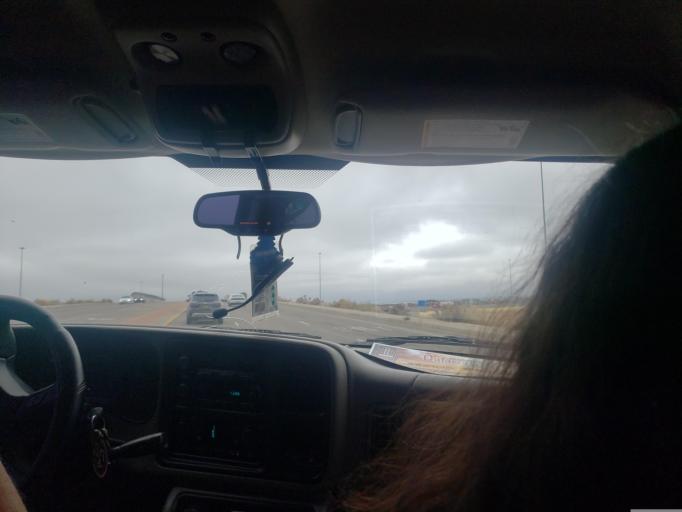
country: US
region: New Mexico
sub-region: Bernalillo County
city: Albuquerque
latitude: 35.0962
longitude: -106.7302
